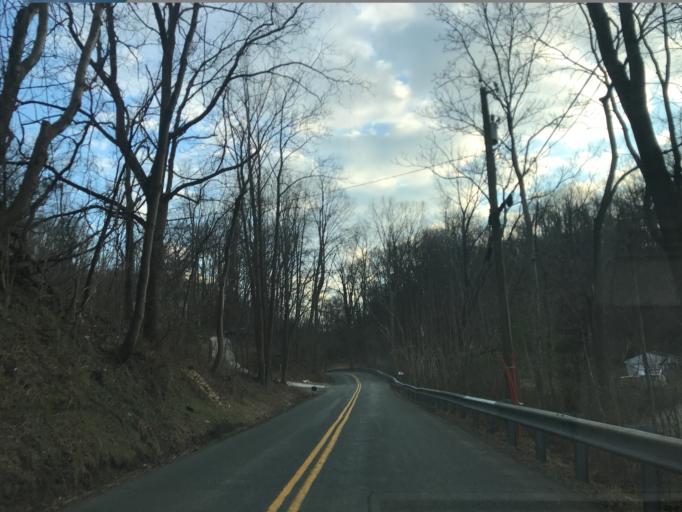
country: US
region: Maryland
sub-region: Harford County
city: Jarrettsville
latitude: 39.6296
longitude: -76.4189
